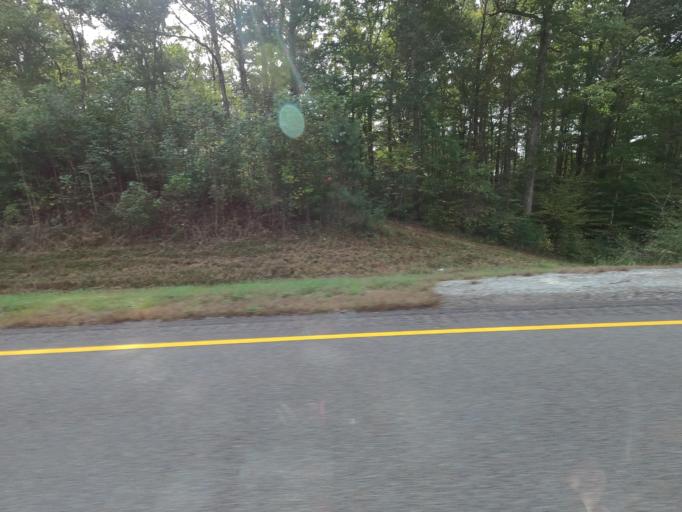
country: US
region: Tennessee
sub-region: Decatur County
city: Parsons
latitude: 35.8159
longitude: -88.2210
